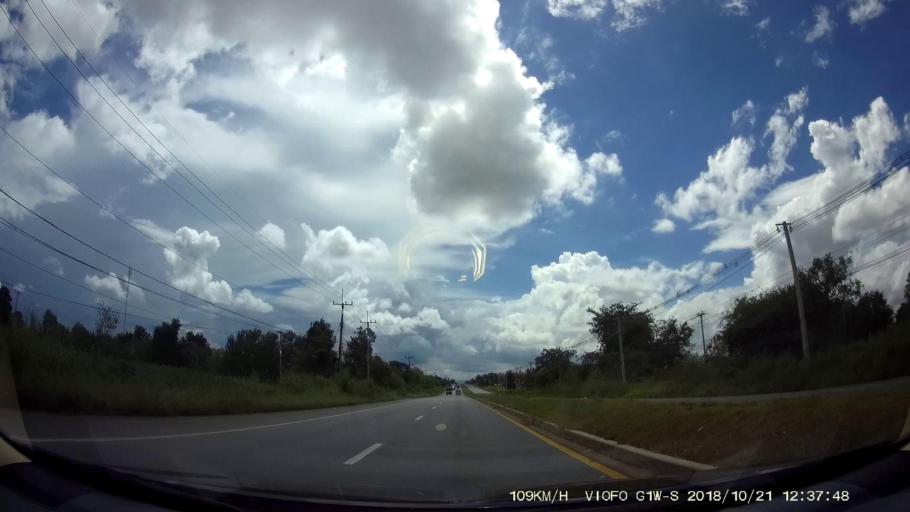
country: TH
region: Nakhon Ratchasima
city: Dan Khun Thot
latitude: 15.0634
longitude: 101.7094
